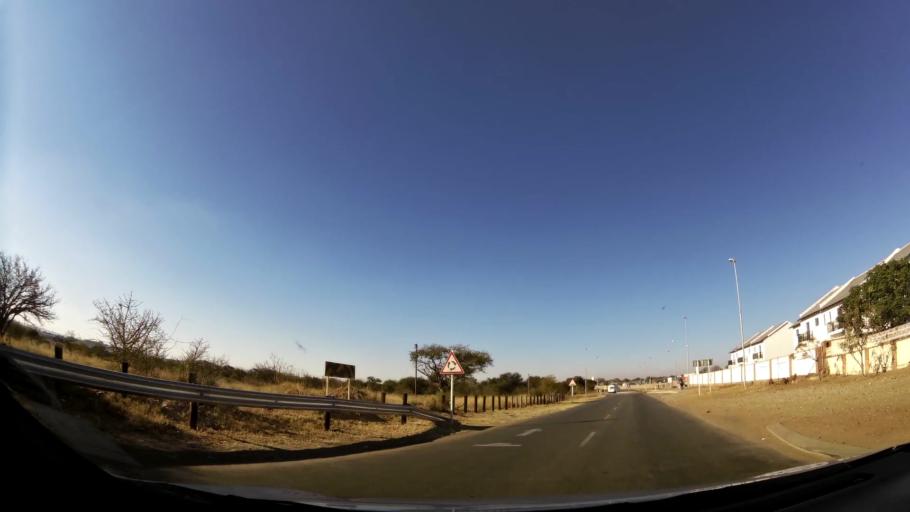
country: ZA
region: Limpopo
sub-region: Capricorn District Municipality
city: Polokwane
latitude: -23.8793
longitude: 29.4732
